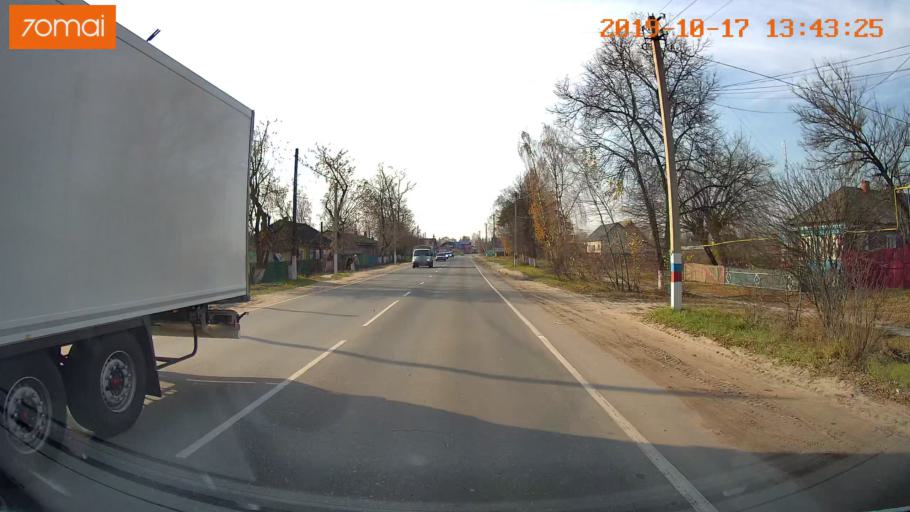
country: RU
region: Rjazan
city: Tuma
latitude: 55.1457
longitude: 40.5449
